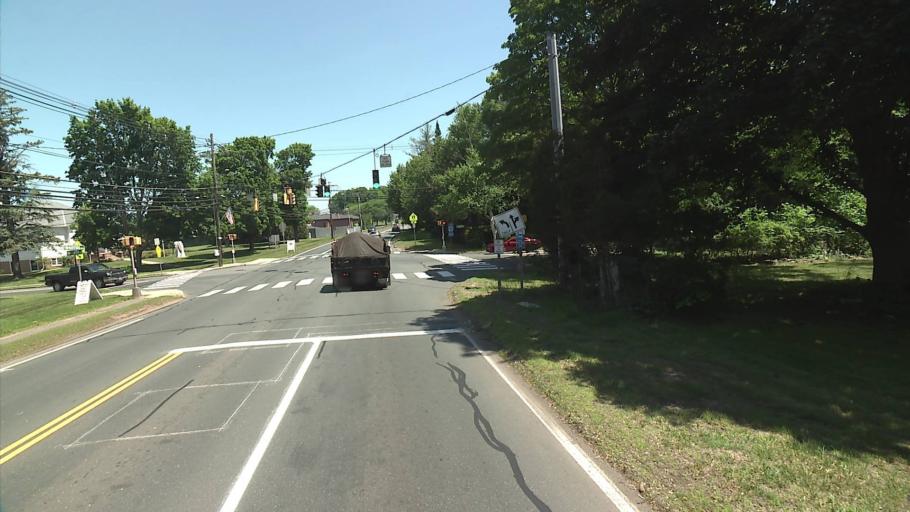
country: US
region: Connecticut
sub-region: Tolland County
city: Rockville
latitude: 41.8380
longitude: -72.4663
